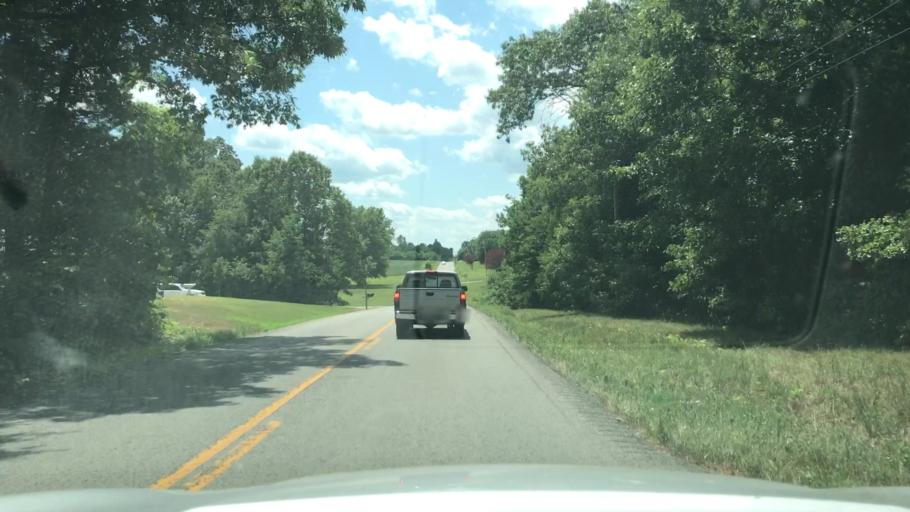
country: US
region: Kentucky
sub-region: Muhlenberg County
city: Greenville
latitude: 37.1727
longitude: -87.2429
